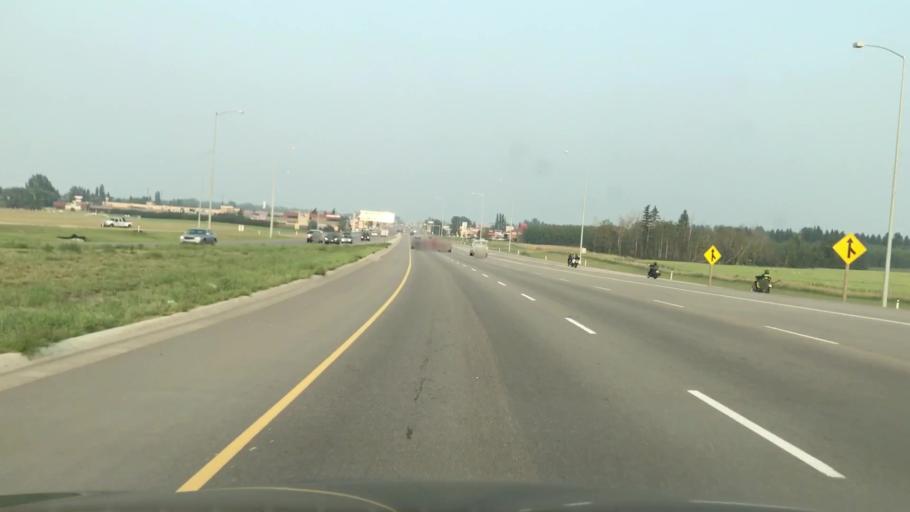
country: CA
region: Alberta
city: Sherwood Park
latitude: 53.5120
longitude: -113.3390
